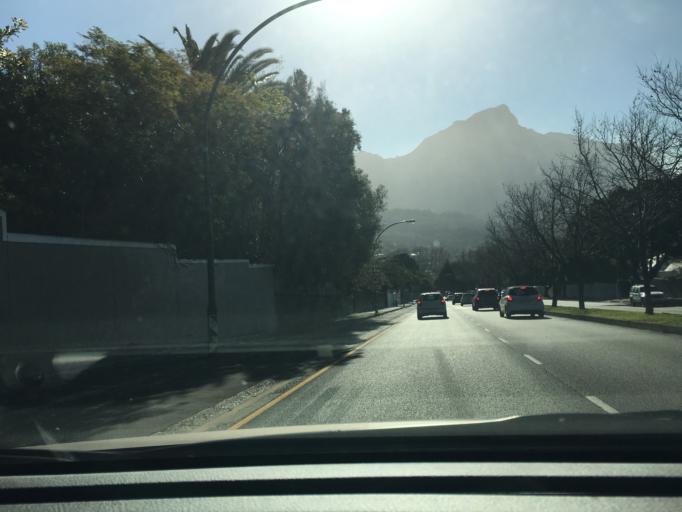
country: ZA
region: Western Cape
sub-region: City of Cape Town
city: Newlands
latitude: -33.9883
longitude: 18.4524
